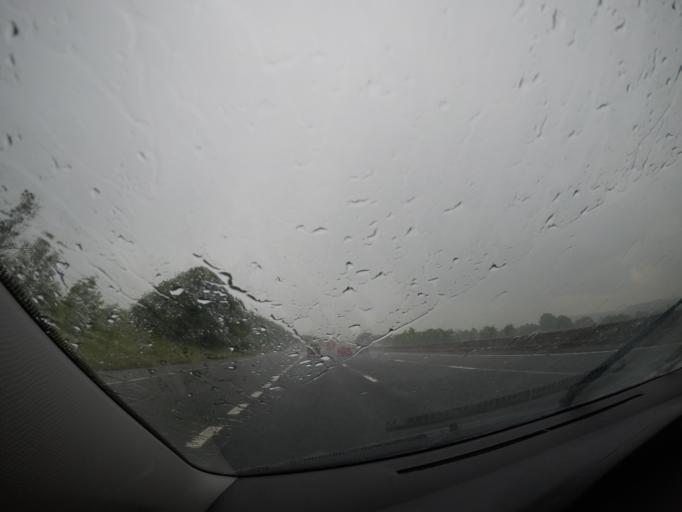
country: GB
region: England
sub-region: Cumbria
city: Penrith
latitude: 54.6895
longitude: -2.7915
